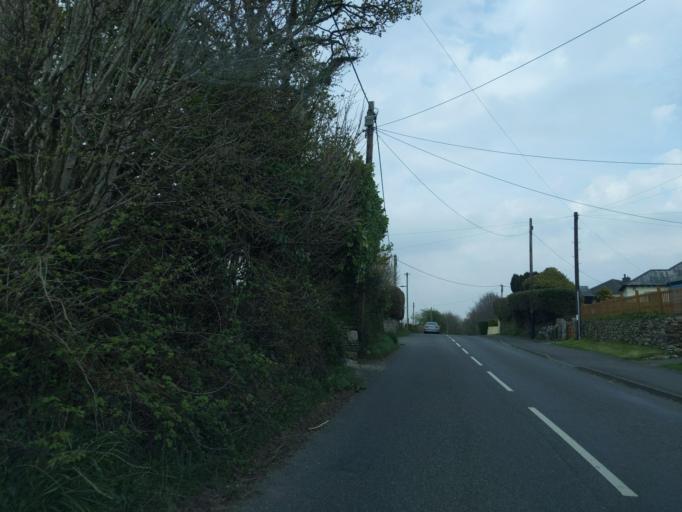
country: GB
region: England
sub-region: Devon
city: Yelverton
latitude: 50.4937
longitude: -4.0815
